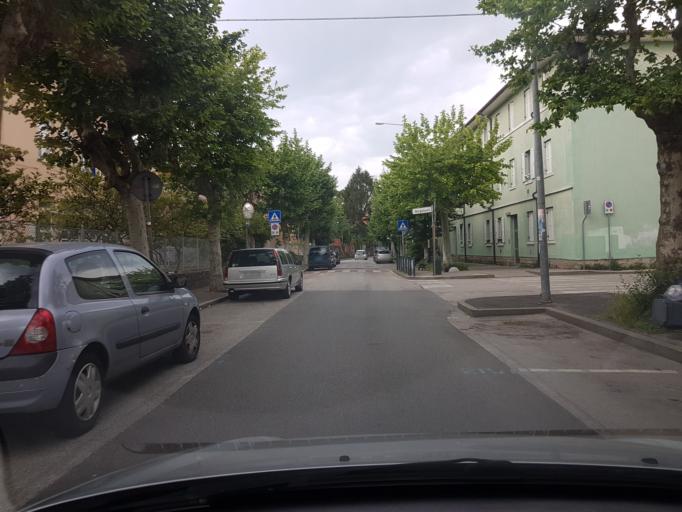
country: IT
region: Friuli Venezia Giulia
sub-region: Provincia di Trieste
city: Muggia
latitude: 45.6011
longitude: 13.7667
